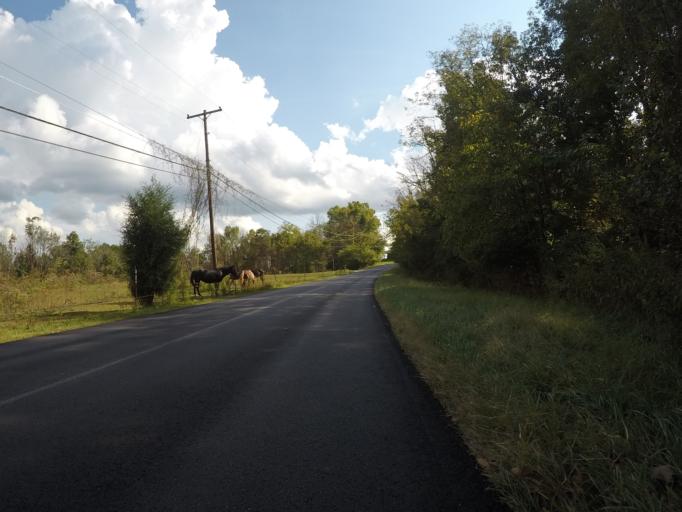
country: US
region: West Virginia
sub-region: Cabell County
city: Huntington
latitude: 38.3791
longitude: -82.4255
